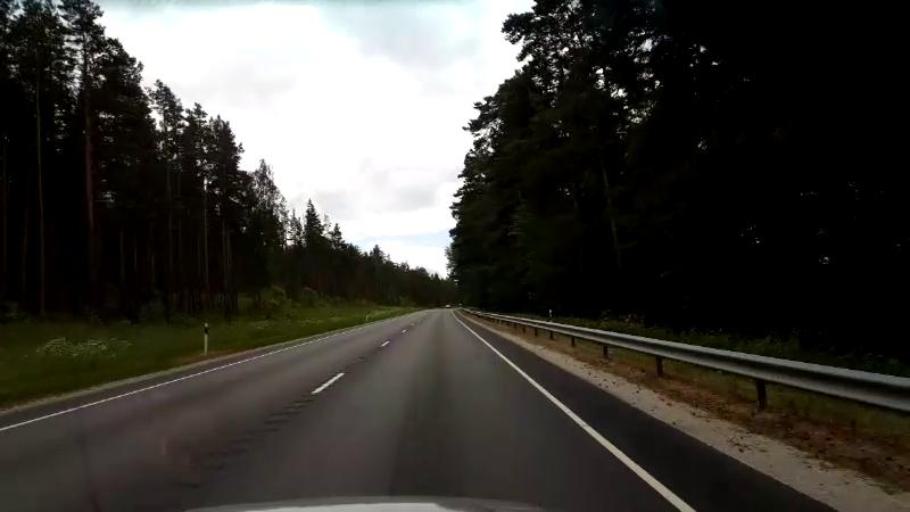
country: EE
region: Paernumaa
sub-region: Paernu linn
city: Parnu
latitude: 58.1553
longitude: 24.4985
